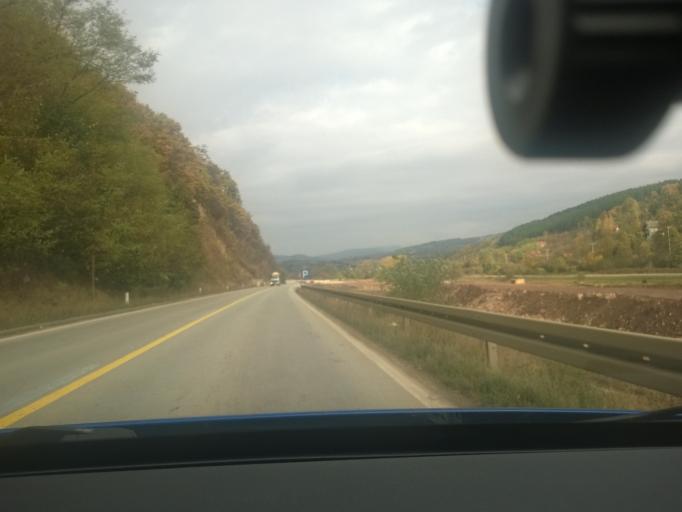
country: RS
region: Central Serbia
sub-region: Pirotski Okrug
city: Pirot
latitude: 43.1984
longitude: 22.5593
